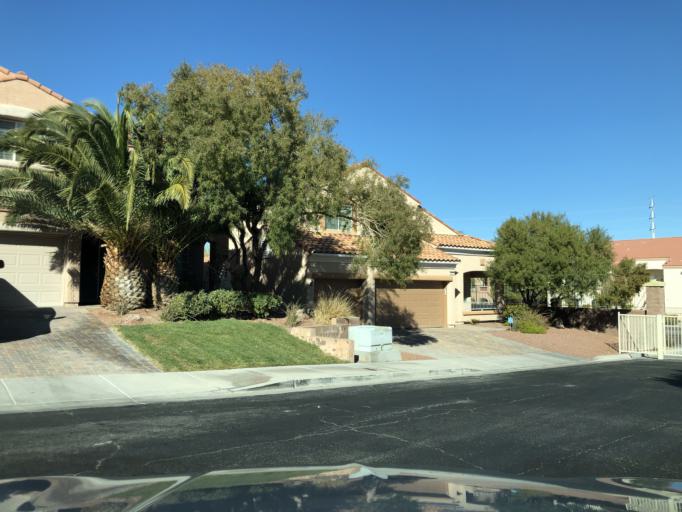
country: US
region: Nevada
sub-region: Clark County
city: Whitney
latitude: 36.0005
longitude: -115.0937
